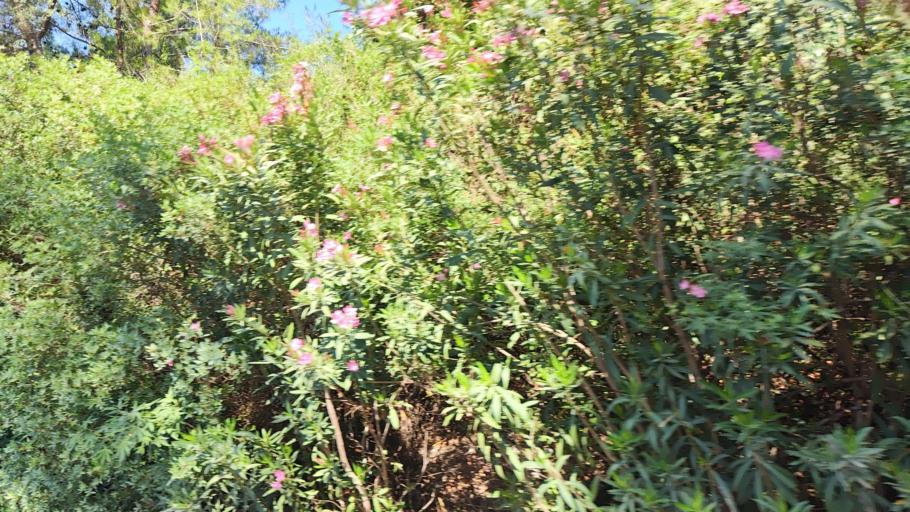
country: TR
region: Mugla
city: Sarigerme
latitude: 36.7053
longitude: 28.6970
